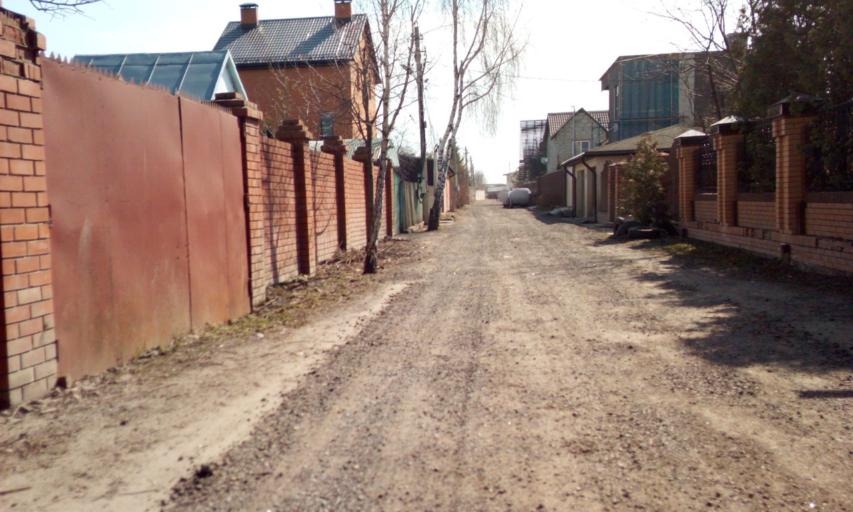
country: RU
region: Moskovskaya
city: Kommunarka
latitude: 55.5212
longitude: 37.4580
